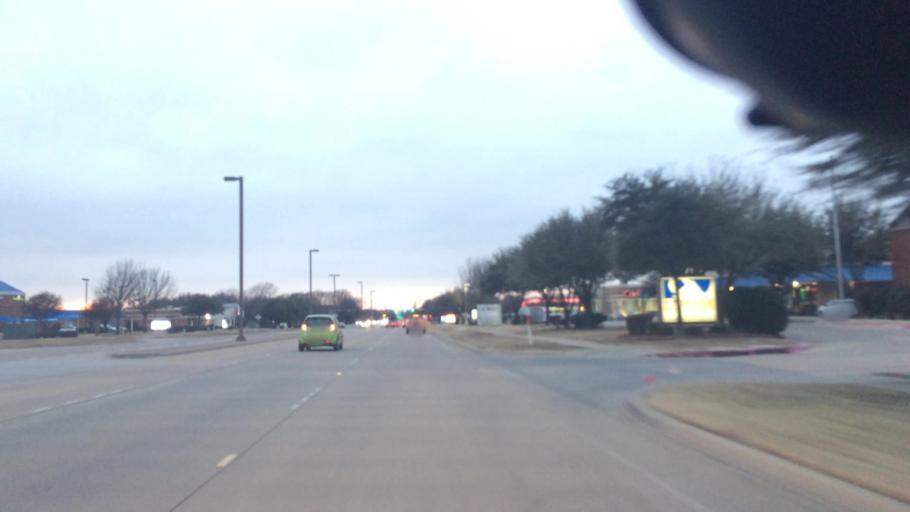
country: US
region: Texas
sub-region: Collin County
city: Allen
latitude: 33.1008
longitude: -96.6947
